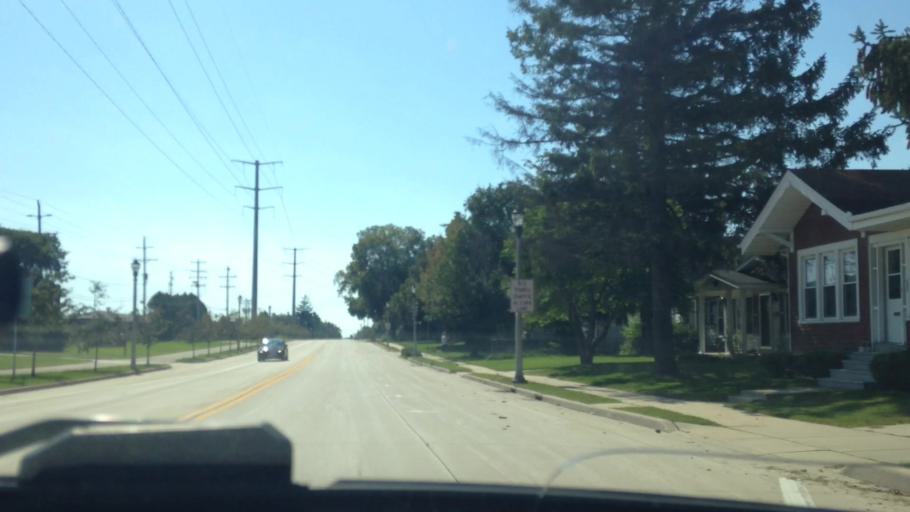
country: US
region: Wisconsin
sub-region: Ozaukee County
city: Port Washington
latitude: 43.3839
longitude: -87.8861
